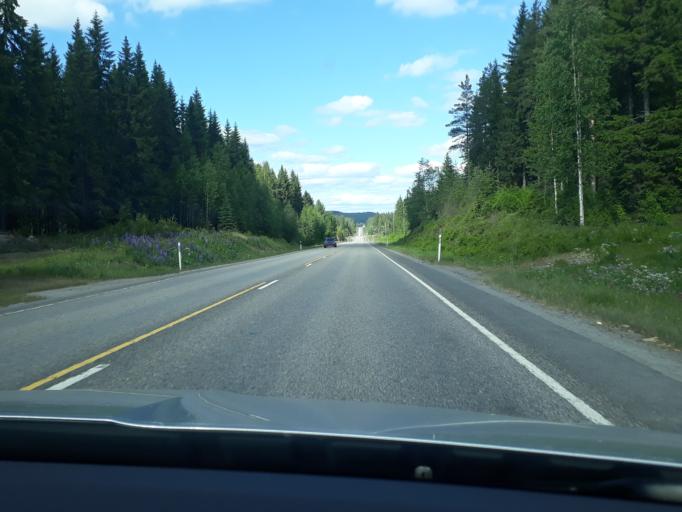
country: FI
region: Central Finland
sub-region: AEaenekoski
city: AEaenekoski
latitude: 62.6503
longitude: 25.7162
